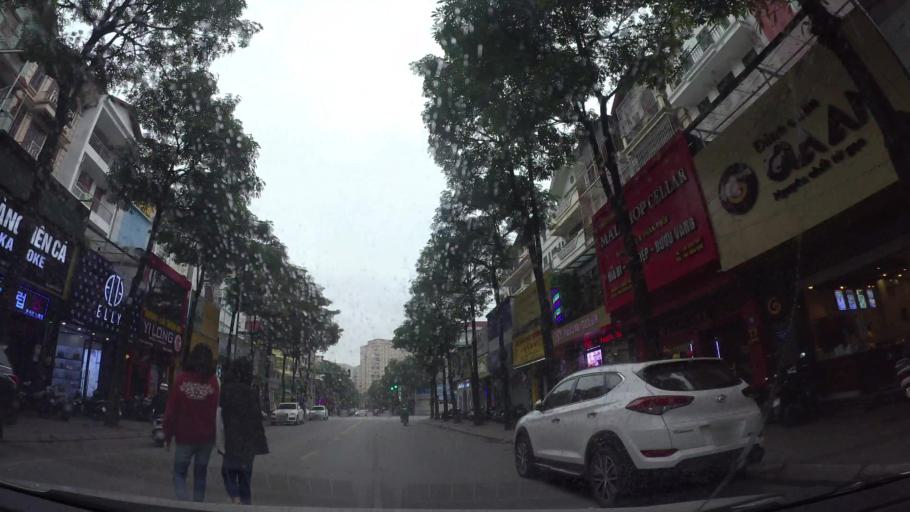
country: VN
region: Ha Noi
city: Cau Giay
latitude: 21.0152
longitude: 105.8012
